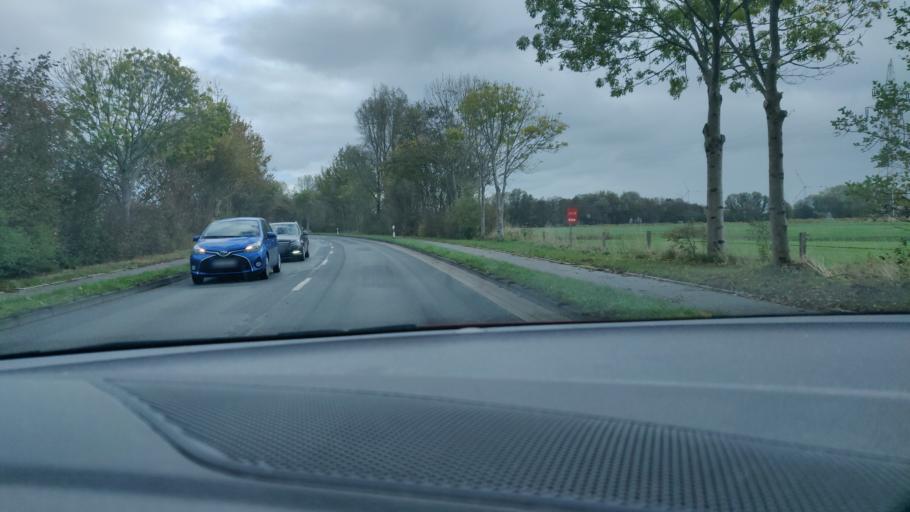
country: DE
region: Lower Saxony
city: Cuxhaven
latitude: 53.8449
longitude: 8.6784
